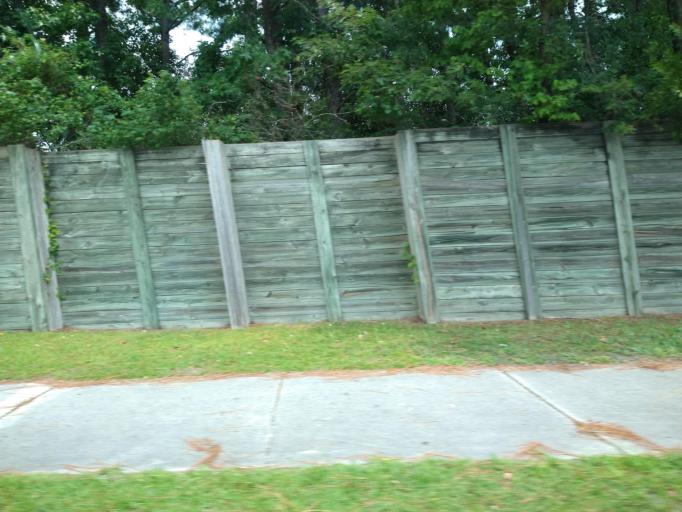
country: US
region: North Carolina
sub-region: Onslow County
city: Pumpkin Center
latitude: 34.7520
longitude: -77.3805
